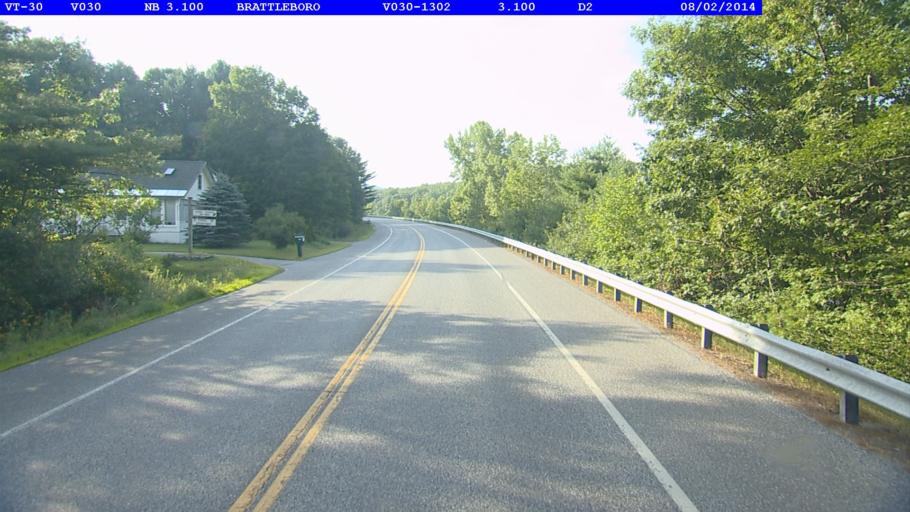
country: US
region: Vermont
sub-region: Windham County
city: West Brattleboro
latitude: 42.8932
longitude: -72.5915
